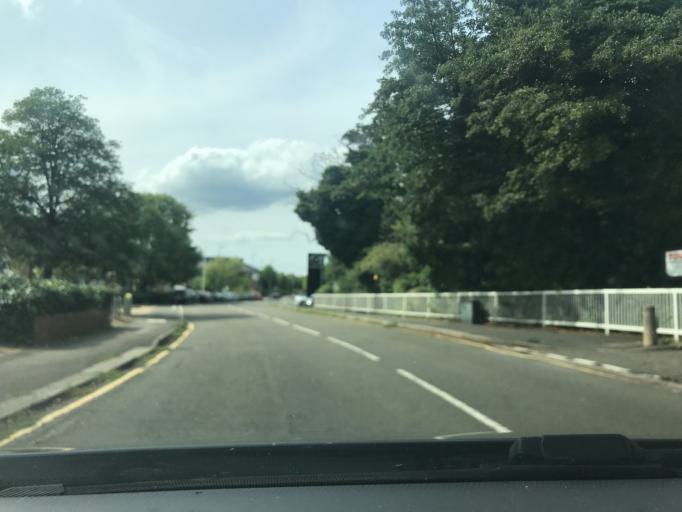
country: GB
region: England
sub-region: Surrey
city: Weybridge
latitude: 51.3719
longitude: -0.4727
